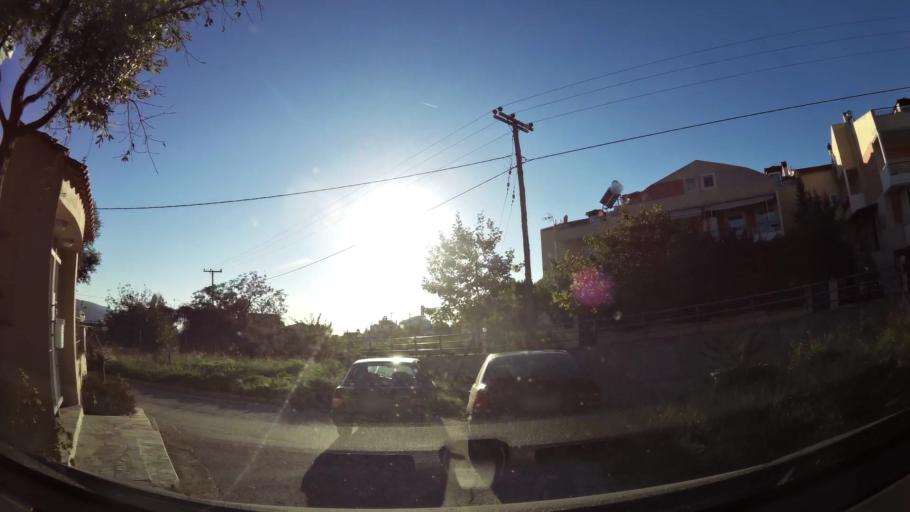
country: GR
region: Attica
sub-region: Nomarchia Athinas
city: Melissia
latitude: 38.0425
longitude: 23.8488
